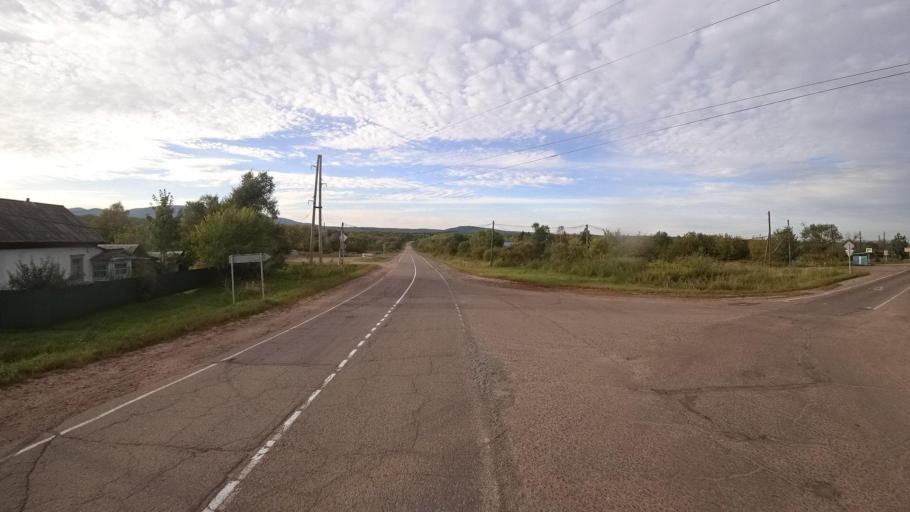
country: RU
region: Primorskiy
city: Yakovlevka
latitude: 44.4176
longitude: 133.4524
